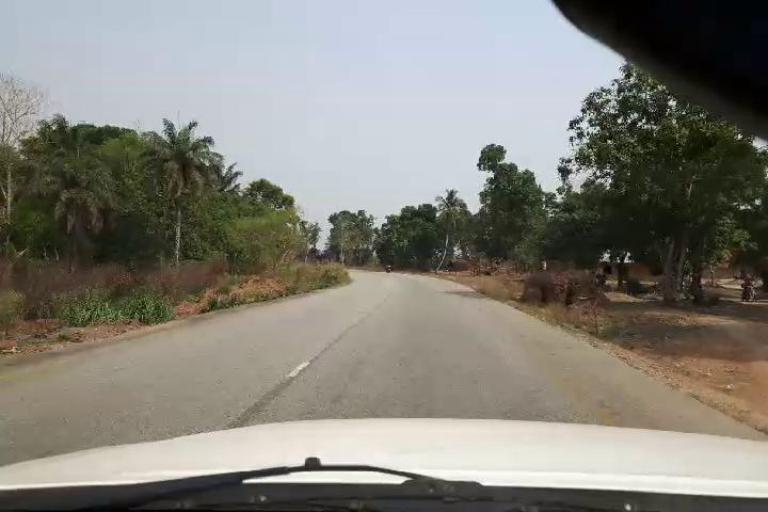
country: SL
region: Southern Province
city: Largo
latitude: 8.3092
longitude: -12.2116
